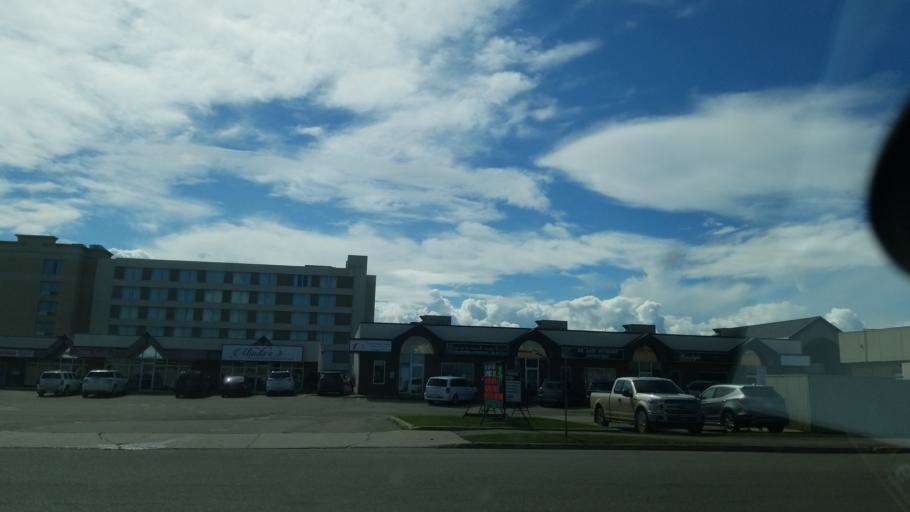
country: CA
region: Saskatchewan
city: Lloydminster
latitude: 53.2771
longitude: -110.0152
